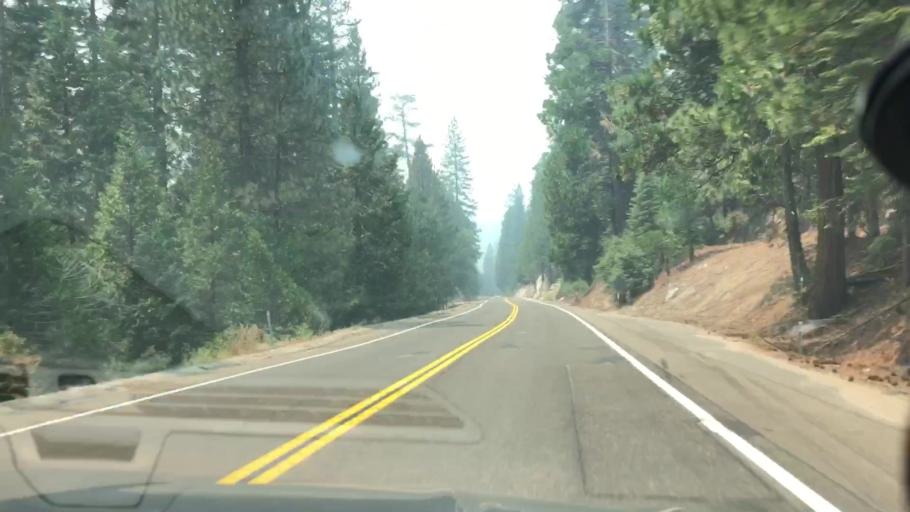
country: US
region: California
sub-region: El Dorado County
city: South Lake Tahoe
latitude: 38.7833
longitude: -120.2265
